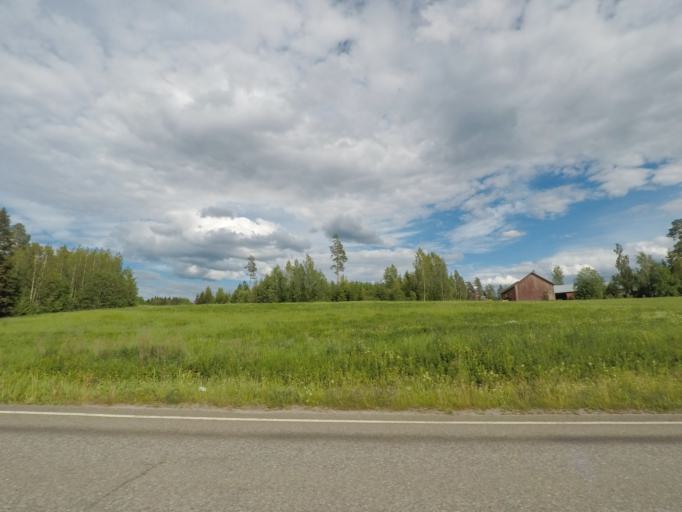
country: FI
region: Paijanne Tavastia
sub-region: Lahti
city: Hollola
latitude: 60.8216
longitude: 25.4864
